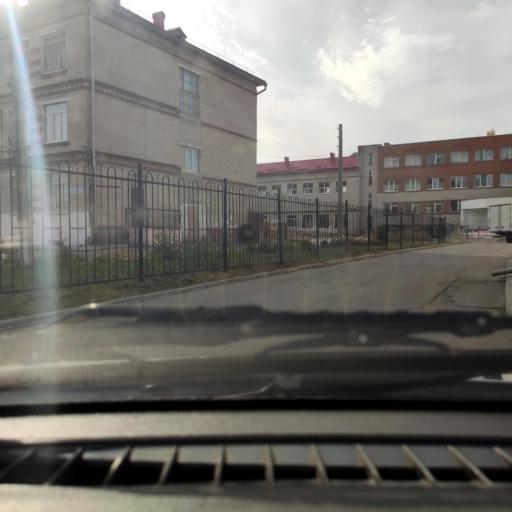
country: RU
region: Samara
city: Tol'yatti
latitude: 53.5100
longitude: 49.4151
